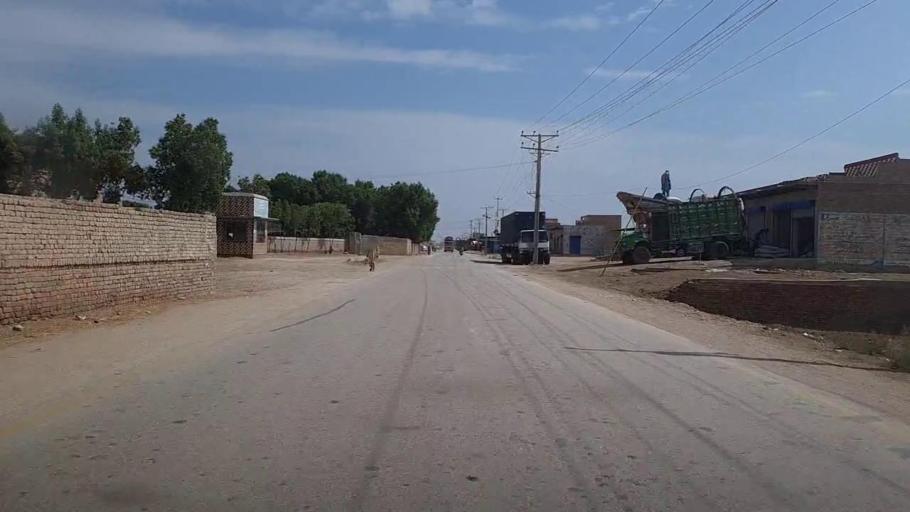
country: PK
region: Sindh
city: Thul
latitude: 28.2470
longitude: 68.7844
